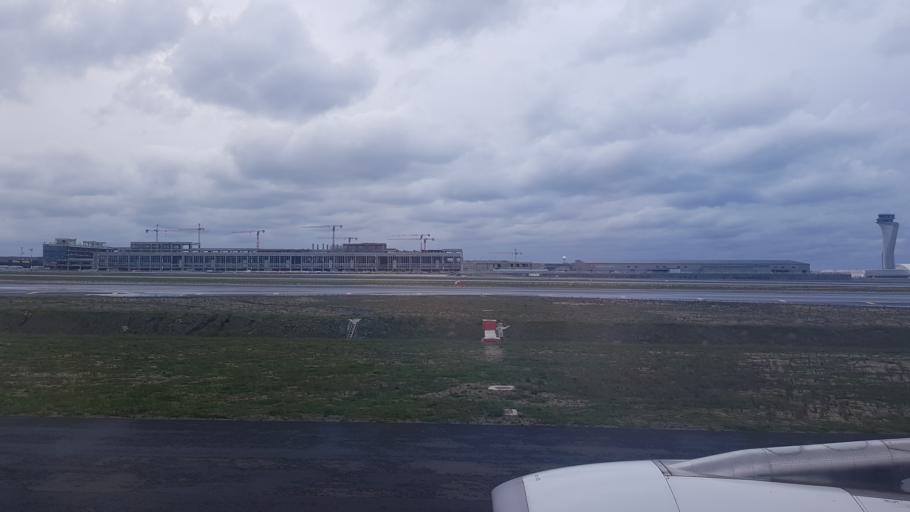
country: TR
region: Istanbul
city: Durusu
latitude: 41.2792
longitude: 28.7296
